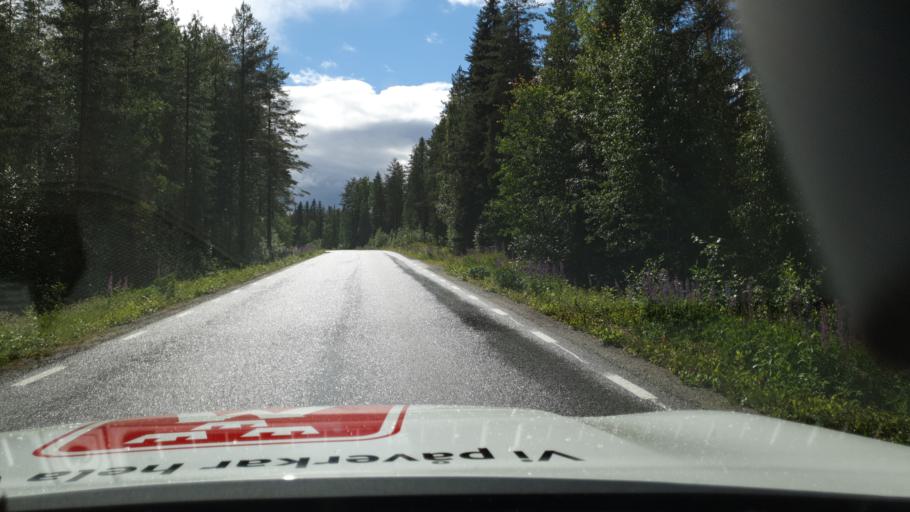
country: SE
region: Vaesterbotten
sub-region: Bjurholms Kommun
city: Bjurholm
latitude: 63.9735
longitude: 19.3123
